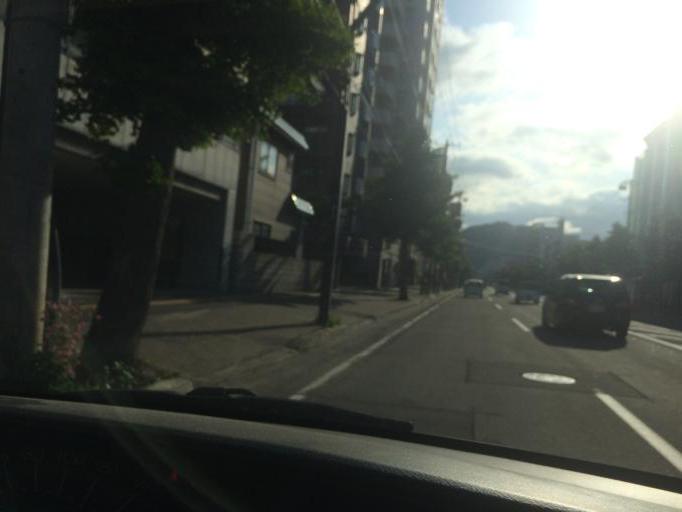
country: JP
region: Hokkaido
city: Sapporo
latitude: 43.0483
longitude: 141.3408
